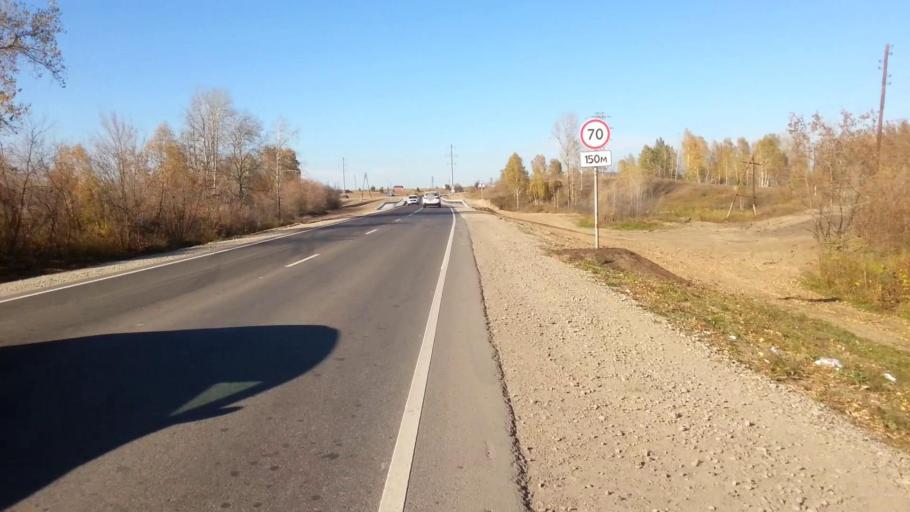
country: RU
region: Altai Krai
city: Sannikovo
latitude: 53.3260
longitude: 83.9421
